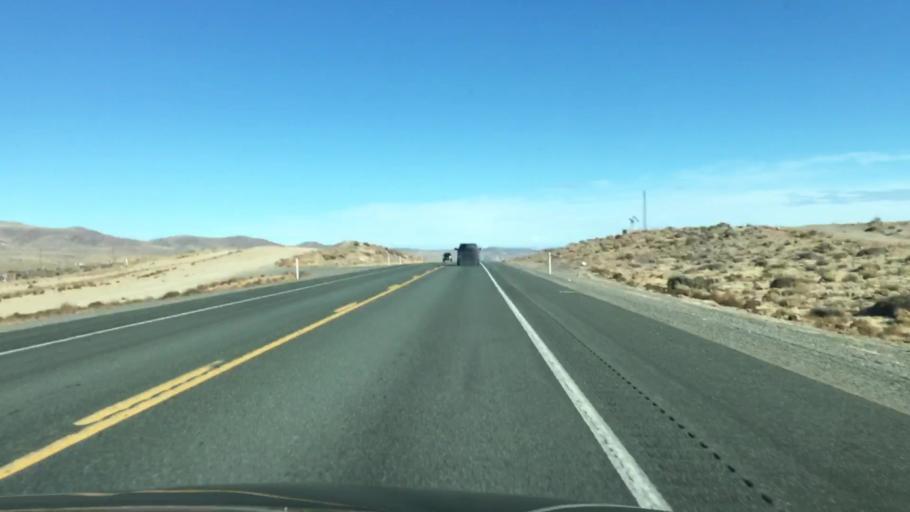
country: US
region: Nevada
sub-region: Lyon County
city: Stagecoach
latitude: 39.3805
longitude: -119.3223
